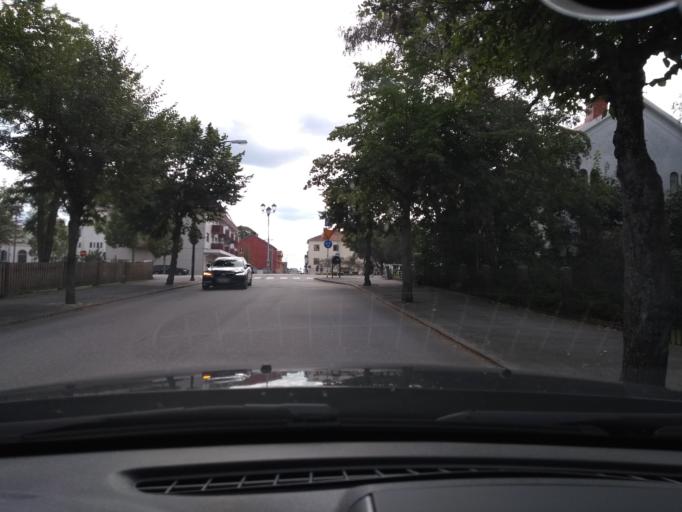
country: SE
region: Kalmar
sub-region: Vimmerby Kommun
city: Vimmerby
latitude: 57.6676
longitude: 15.8572
